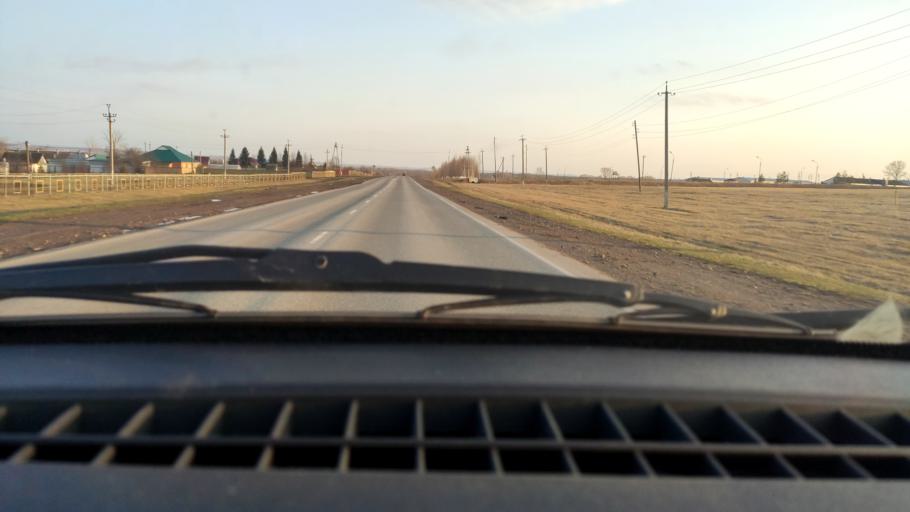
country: RU
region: Bashkortostan
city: Davlekanovo
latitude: 54.3794
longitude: 55.1957
